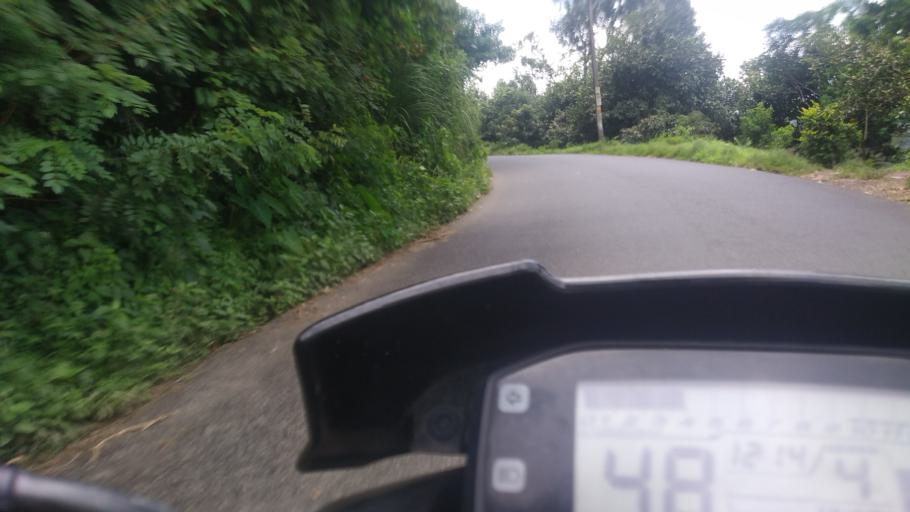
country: IN
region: Kerala
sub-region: Idukki
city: Munnar
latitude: 10.0147
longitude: 77.0056
